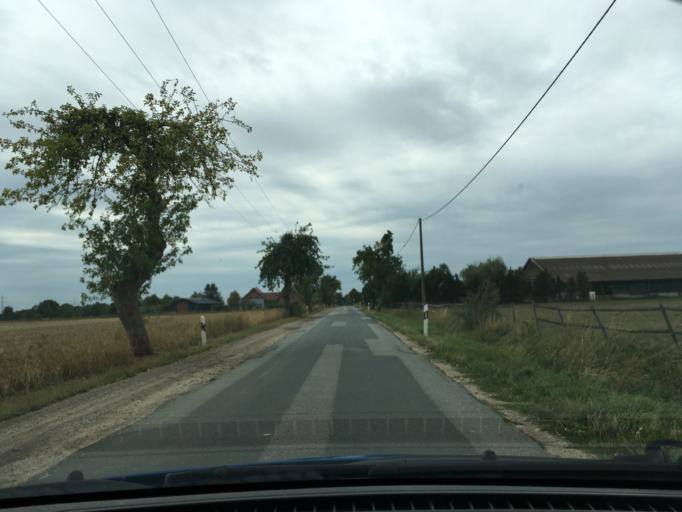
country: DE
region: Mecklenburg-Vorpommern
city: Wittenburg
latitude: 53.5149
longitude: 11.1438
